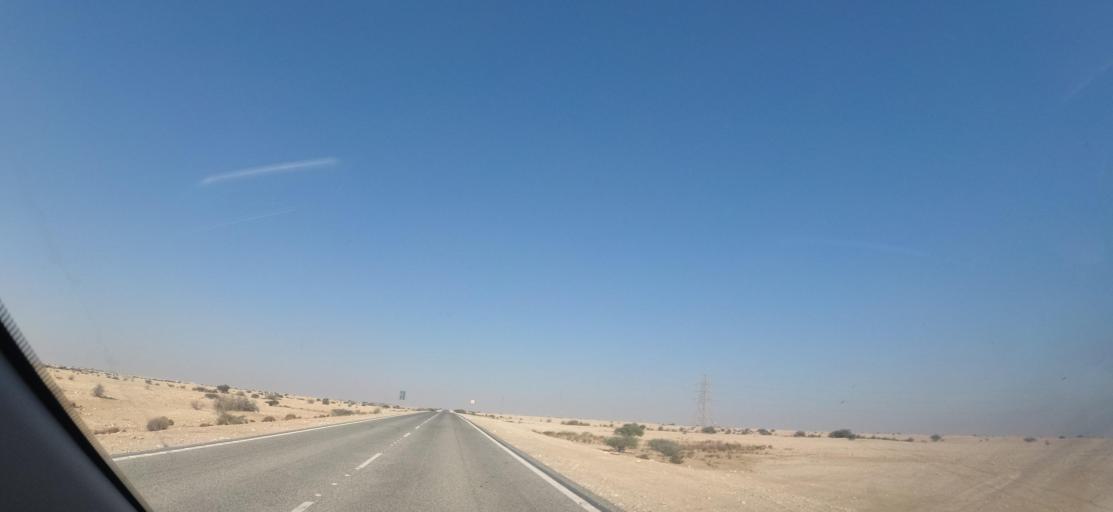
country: QA
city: Al Jumayliyah
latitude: 25.6314
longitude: 51.0958
